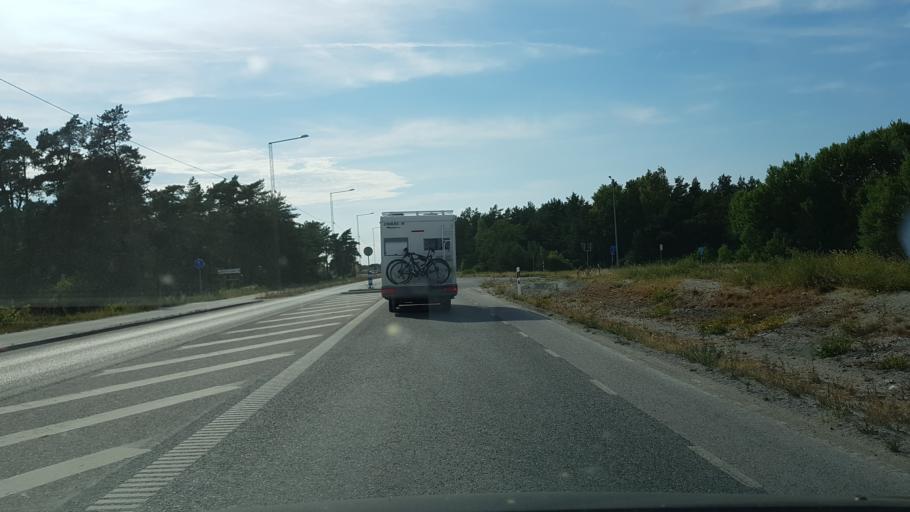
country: SE
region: Gotland
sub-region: Gotland
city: Visby
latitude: 57.6315
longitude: 18.3352
